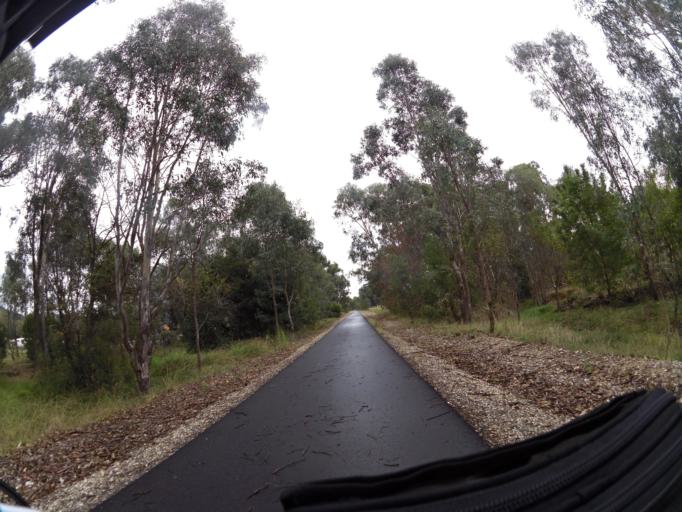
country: AU
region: Victoria
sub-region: Wodonga
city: Wodonga
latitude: -36.1462
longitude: 146.9211
